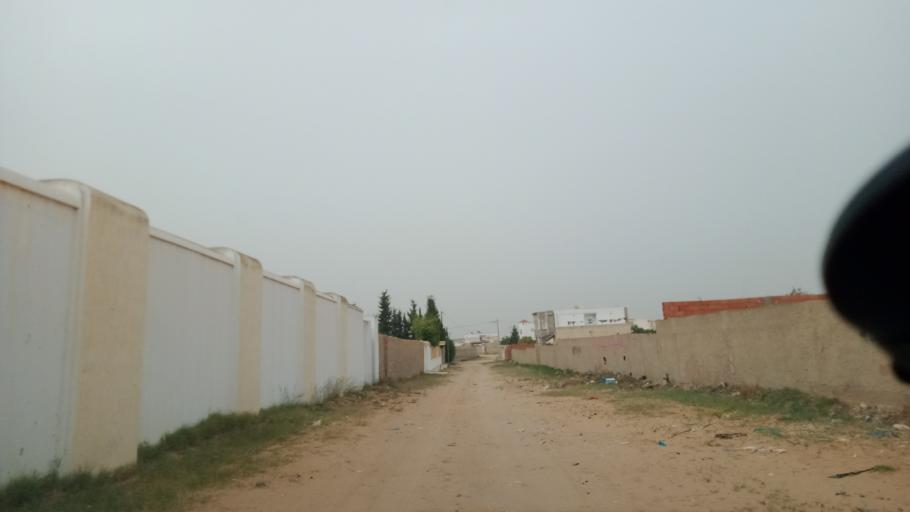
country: TN
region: Safaqis
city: Al Qarmadah
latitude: 34.7903
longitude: 10.7636
